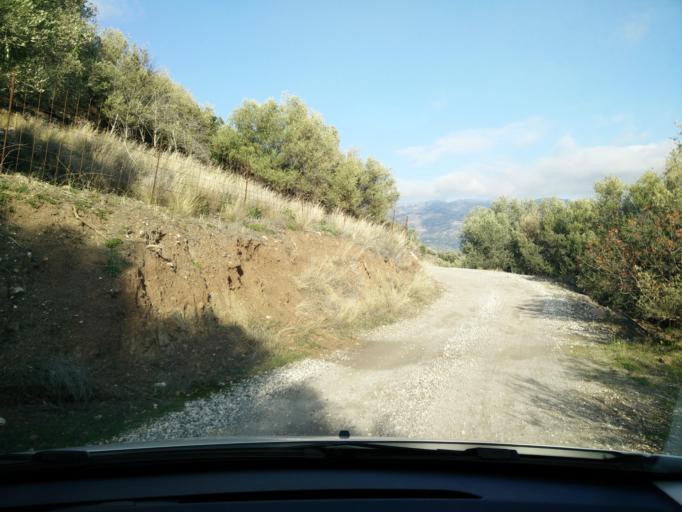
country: GR
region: Crete
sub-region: Nomos Lasithiou
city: Gra Liyia
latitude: 35.0306
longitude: 25.5671
